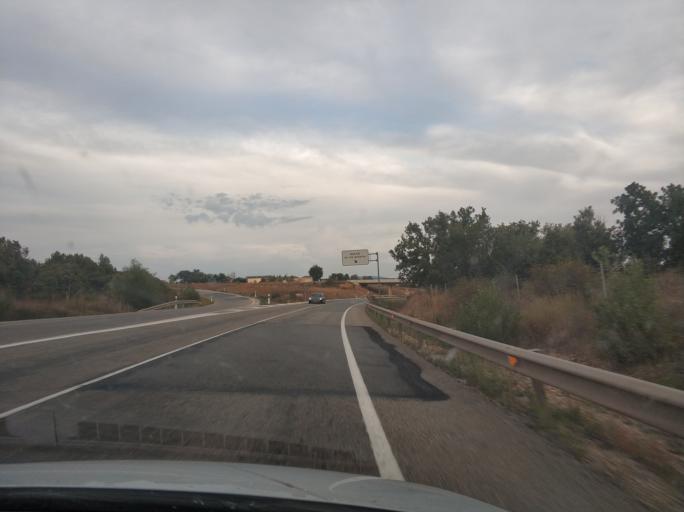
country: ES
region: Castille and Leon
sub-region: Provincia de Burgos
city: Salas de los Infantes
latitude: 42.0210
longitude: -3.3069
